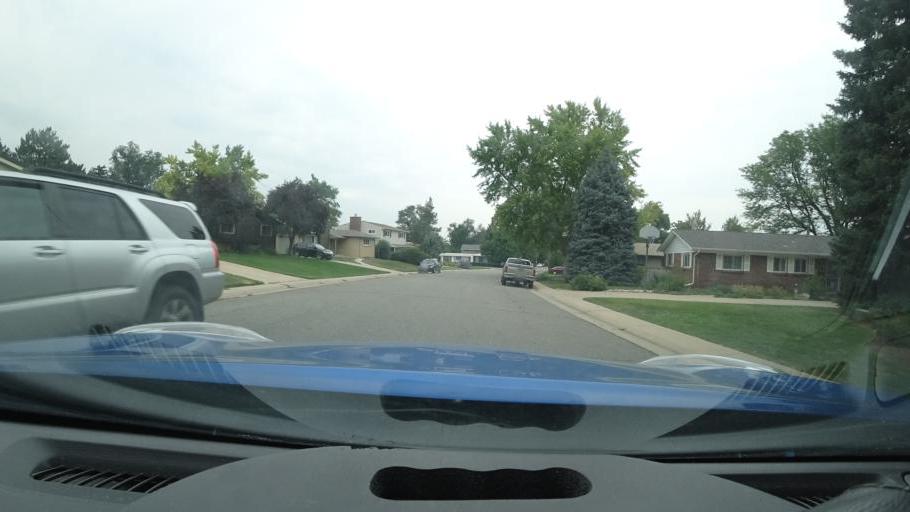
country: US
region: Colorado
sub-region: Arapahoe County
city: Glendale
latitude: 39.6866
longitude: -104.9152
